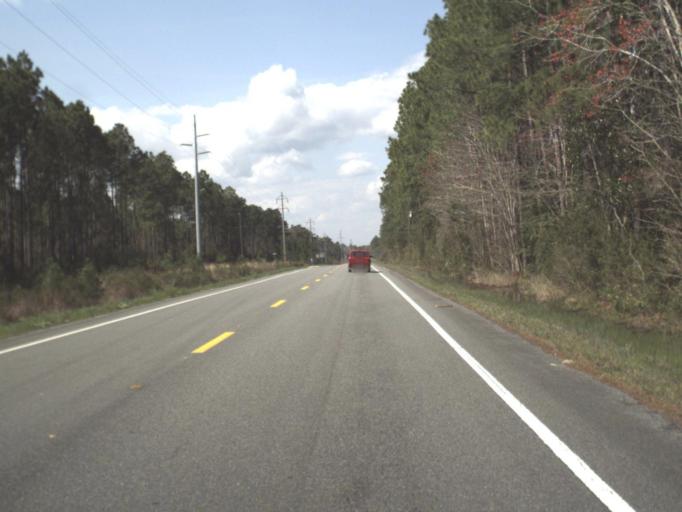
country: US
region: Florida
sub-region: Franklin County
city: Carrabelle
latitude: 29.9809
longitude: -84.5006
